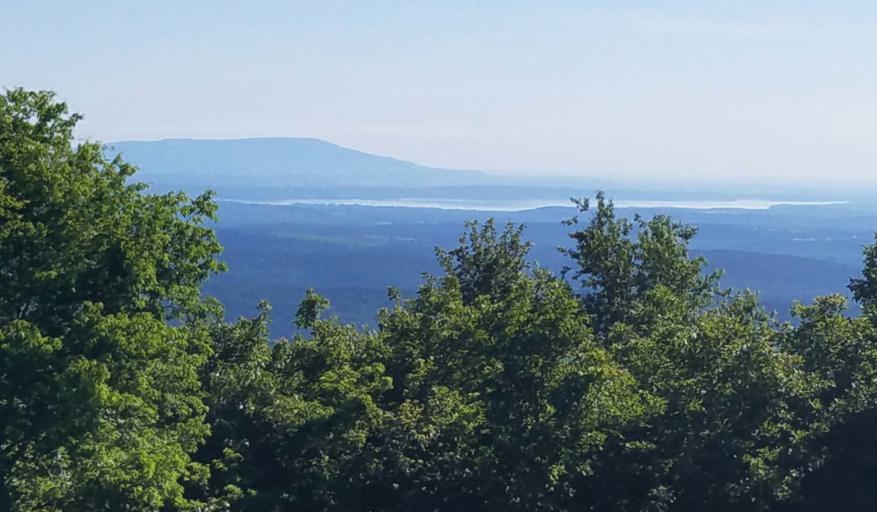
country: US
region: Oklahoma
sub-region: Le Flore County
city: Talihina
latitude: 34.7952
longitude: -94.9262
